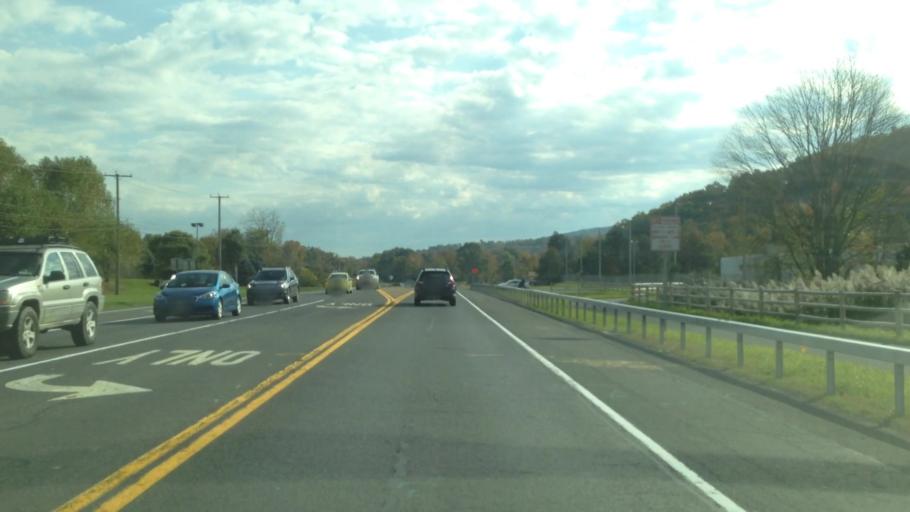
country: US
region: New York
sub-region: Ulster County
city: Clintondale
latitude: 41.7378
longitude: -74.0360
